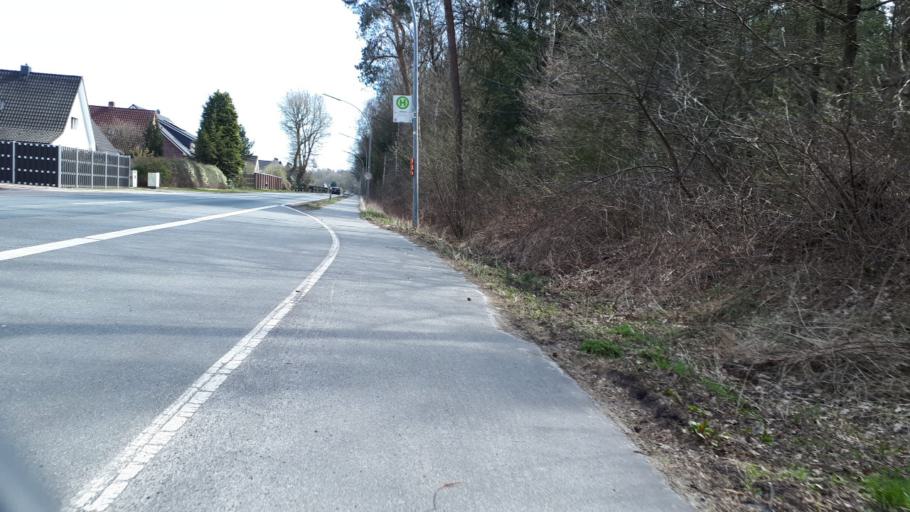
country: DE
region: Lower Saxony
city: Wardenburg
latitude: 53.0451
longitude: 8.2709
